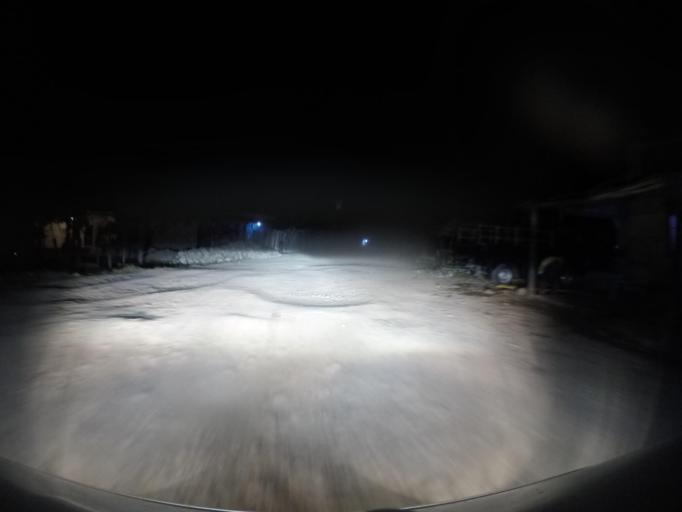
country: TL
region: Viqueque
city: Viqueque
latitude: -8.7954
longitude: 126.5573
